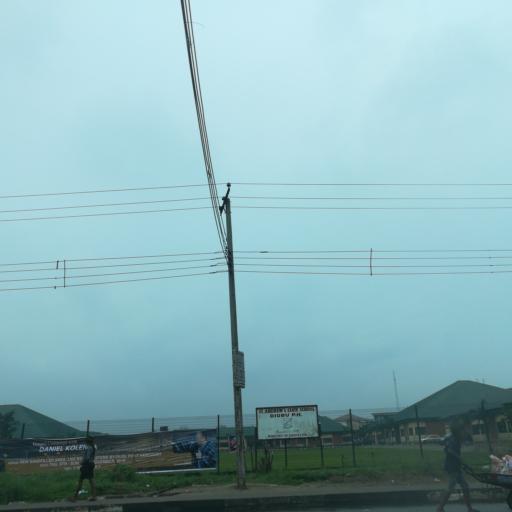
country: NG
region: Rivers
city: Port Harcourt
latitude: 4.7930
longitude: 6.9964
